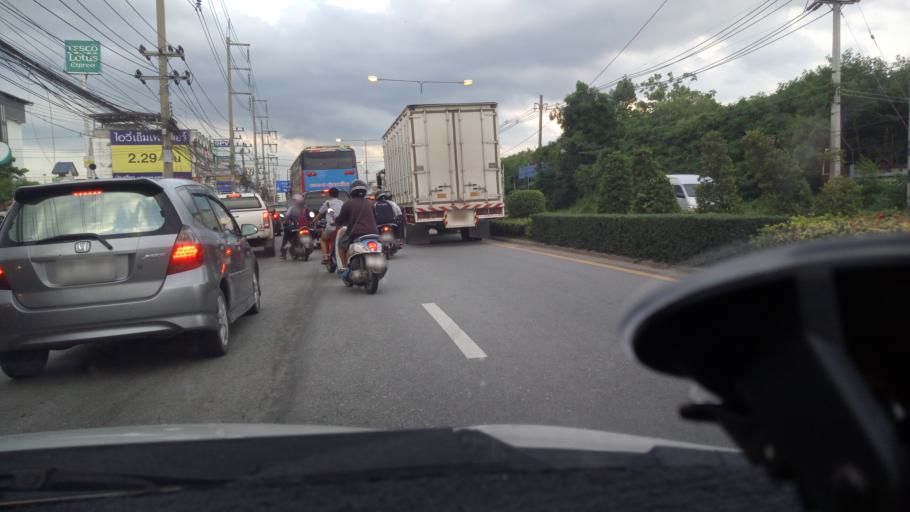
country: TH
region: Chon Buri
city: Chon Buri
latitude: 13.4053
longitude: 101.0427
